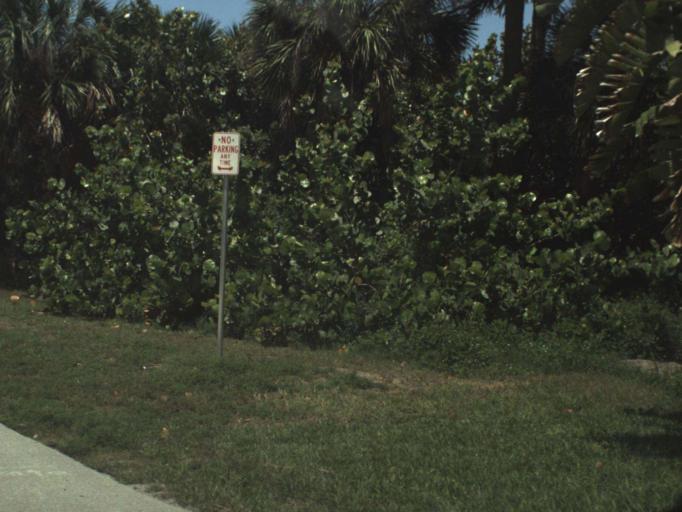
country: US
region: Florida
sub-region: Brevard County
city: Indialantic
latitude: 28.0828
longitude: -80.5635
